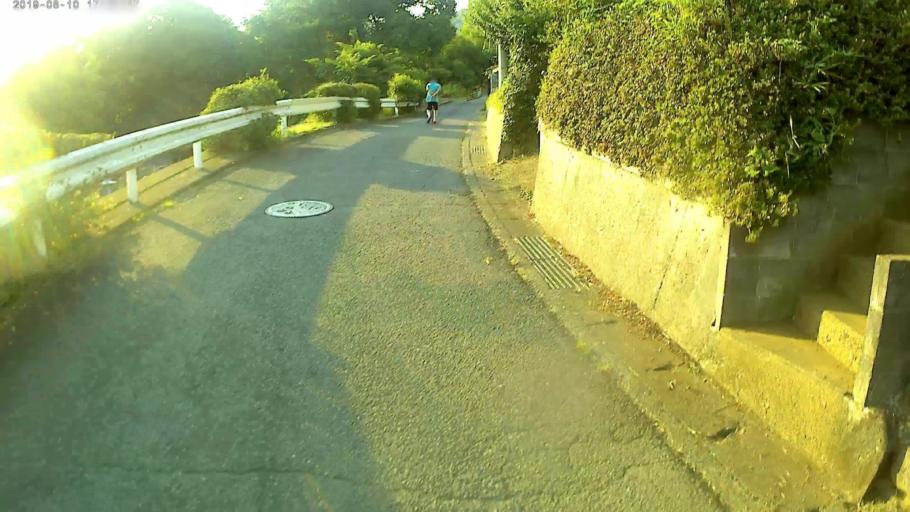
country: JP
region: Yamanashi
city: Uenohara
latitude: 35.6193
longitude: 139.1698
